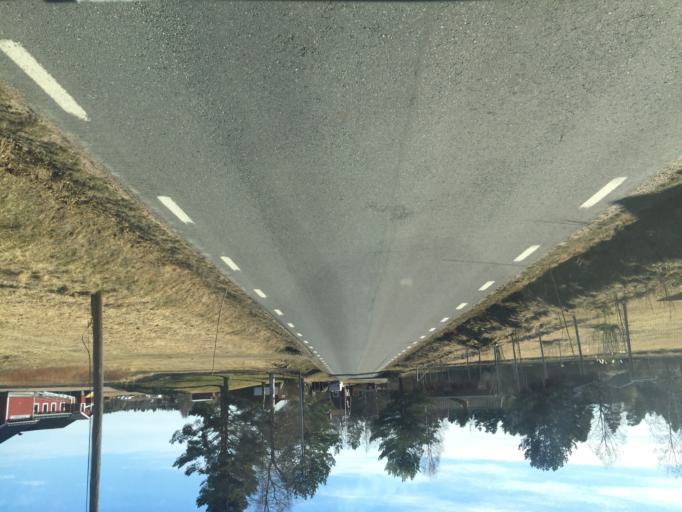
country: SE
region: Dalarna
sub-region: Vansbro Kommun
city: Vansbro
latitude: 60.4607
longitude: 13.9850
